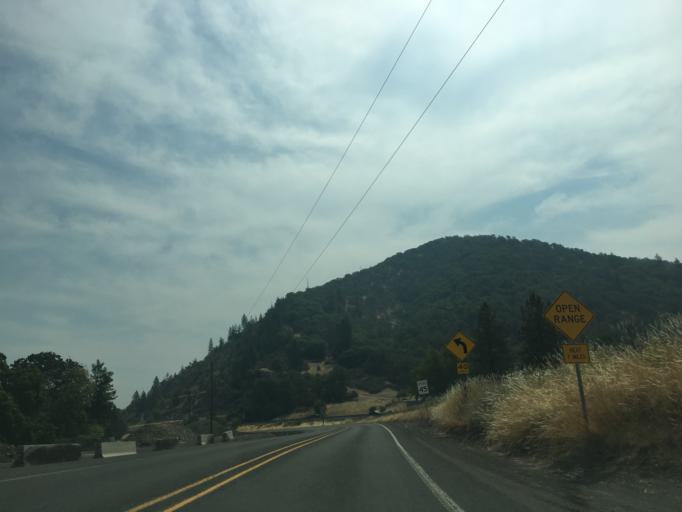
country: US
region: Oregon
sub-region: Jackson County
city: Gold Hill
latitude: 42.4303
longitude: -123.0960
